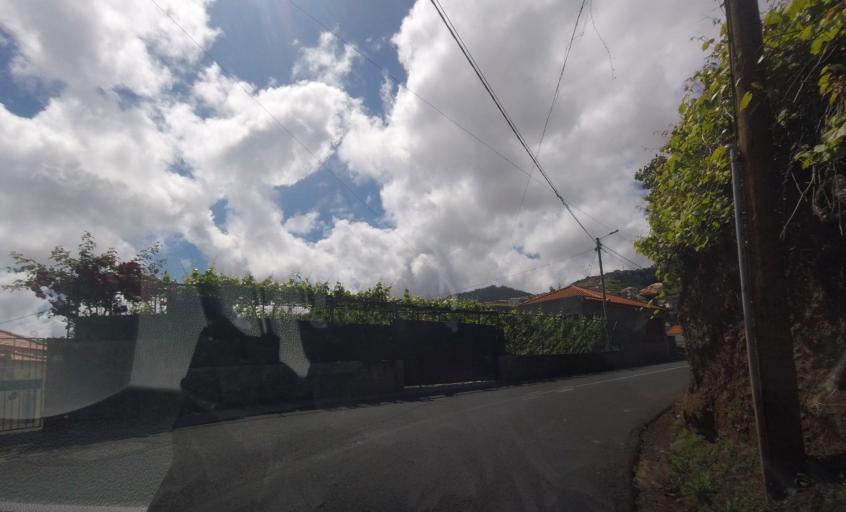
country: PT
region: Madeira
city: Camara de Lobos
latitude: 32.6736
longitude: -16.9748
